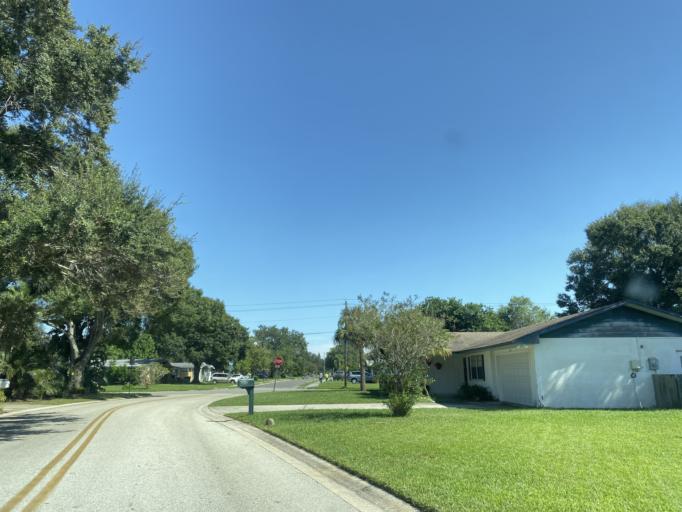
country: US
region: Florida
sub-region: Manatee County
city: South Bradenton
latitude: 27.4806
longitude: -82.5964
